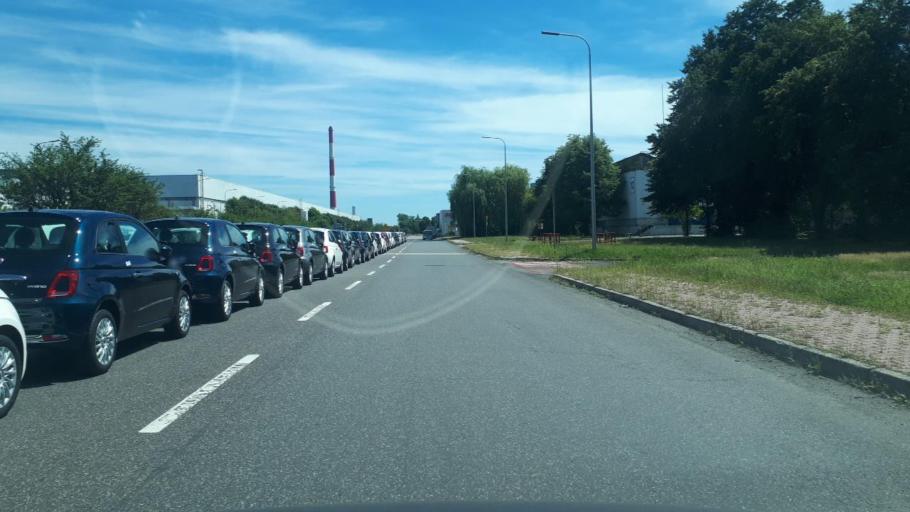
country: PL
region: Silesian Voivodeship
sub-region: Powiat bierunsko-ledzinski
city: Bierun
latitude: 50.1041
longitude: 19.0738
